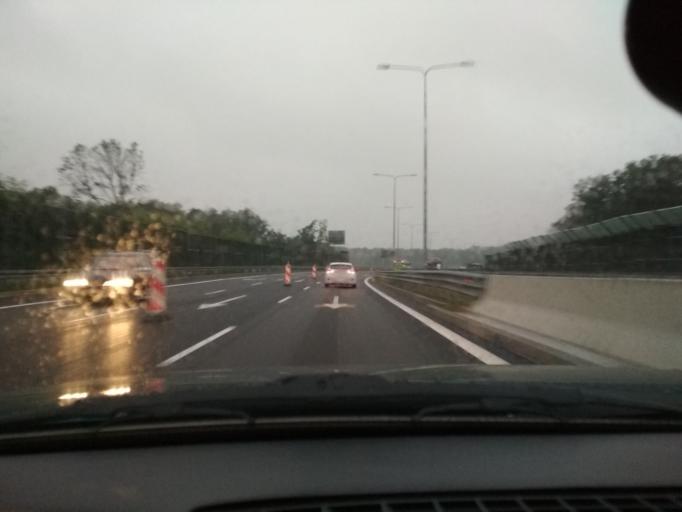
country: PL
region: Silesian Voivodeship
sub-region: Zabrze
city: Zabrze
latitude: 50.2880
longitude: 18.7796
